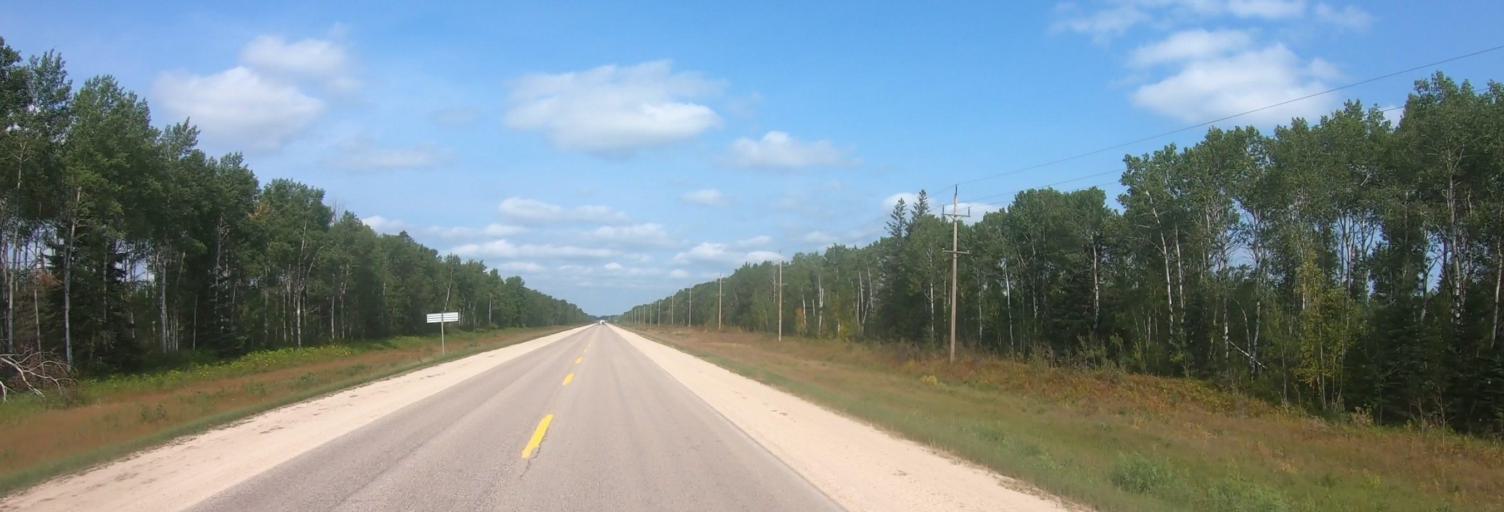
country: CA
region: Manitoba
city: La Broquerie
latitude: 49.1951
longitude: -96.2633
